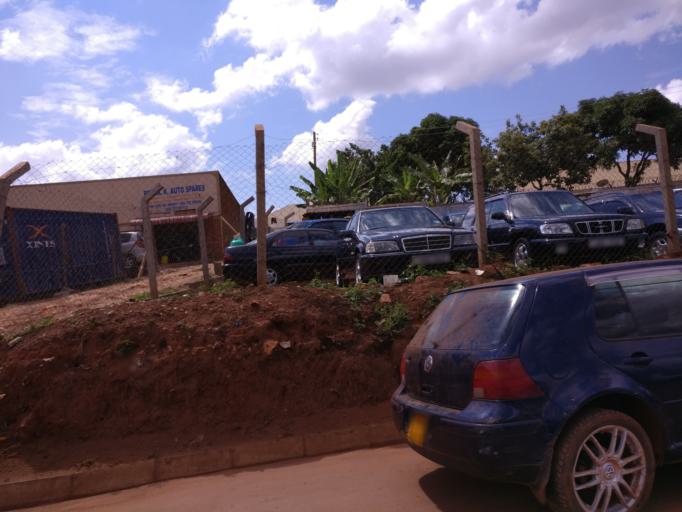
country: UG
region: Central Region
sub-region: Kampala District
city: Kampala
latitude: 0.2858
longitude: 32.5626
